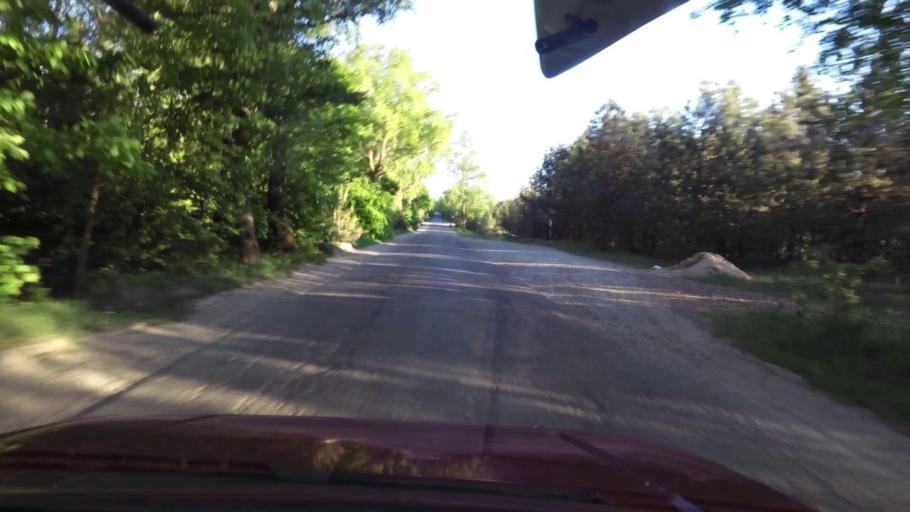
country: PL
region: West Pomeranian Voivodeship
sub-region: Powiat szczecinecki
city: Bialy Bor
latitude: 53.9198
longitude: 16.8050
